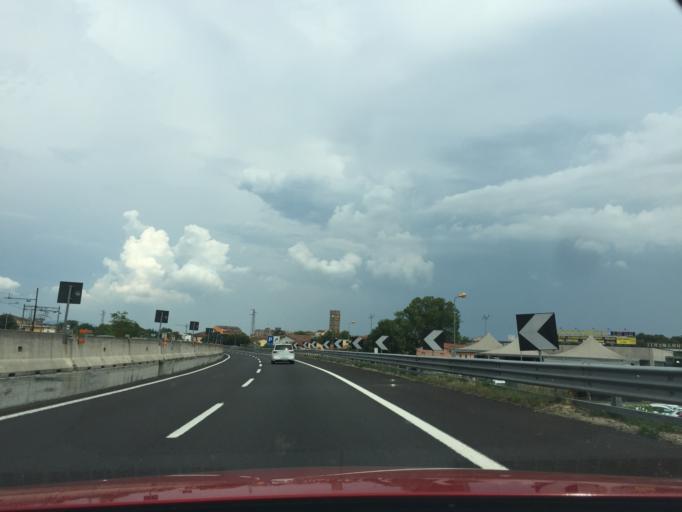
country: IT
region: Tuscany
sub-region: Provincia di Lucca
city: Altopascio
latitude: 43.8146
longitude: 10.6671
